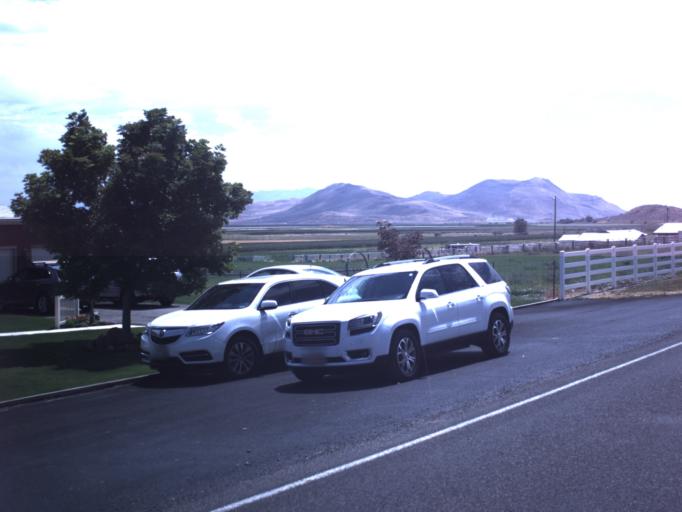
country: US
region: Utah
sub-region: Box Elder County
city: Tremonton
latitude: 41.6674
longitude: -112.2965
